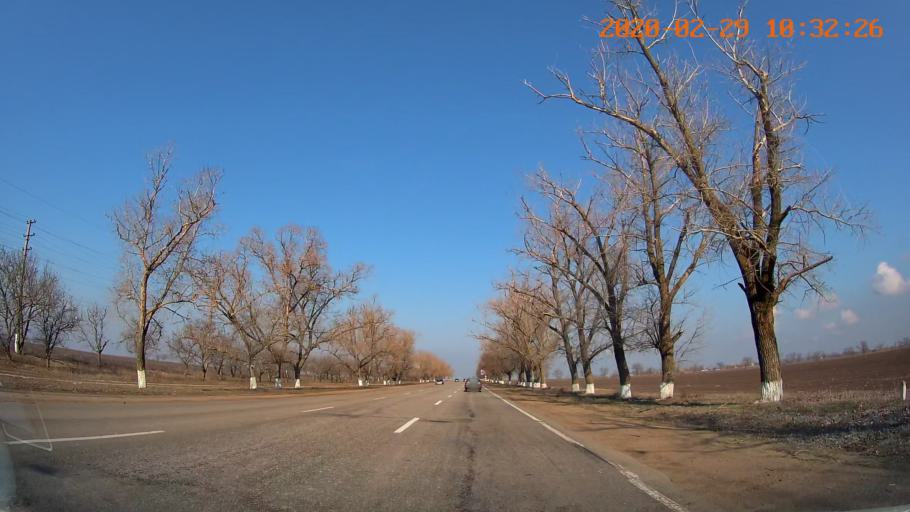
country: UA
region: Odessa
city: Velykoploske
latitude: 46.9610
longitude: 29.5539
